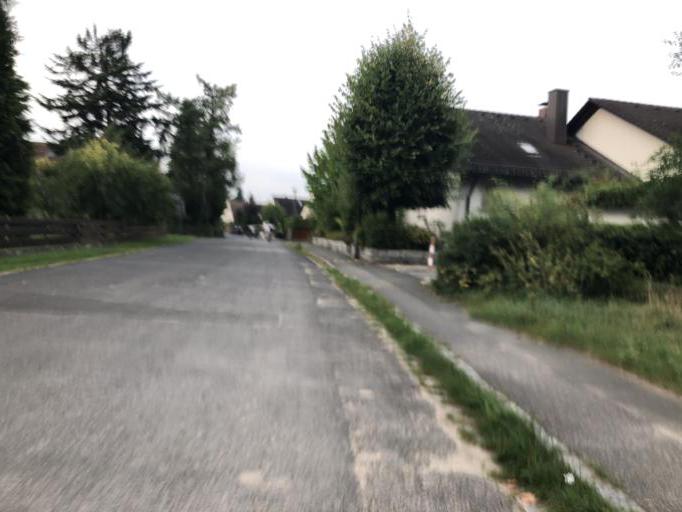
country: DE
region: Bavaria
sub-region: Regierungsbezirk Mittelfranken
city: Erlangen
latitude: 49.5558
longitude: 11.0265
